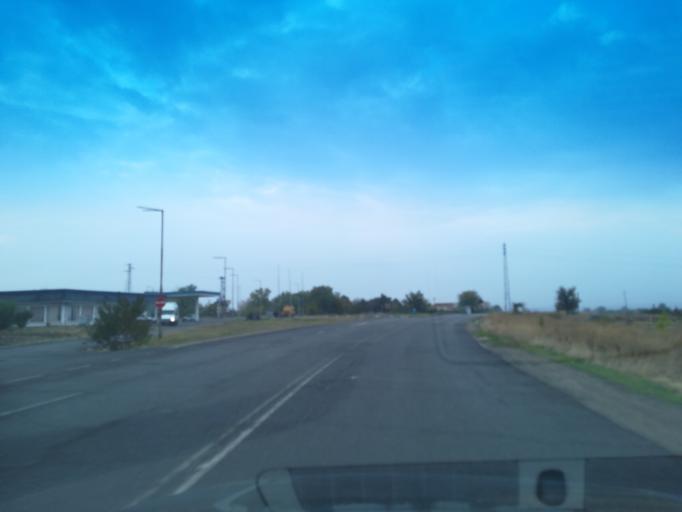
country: BG
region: Stara Zagora
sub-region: Obshtina Chirpan
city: Chirpan
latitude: 42.1951
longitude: 25.3129
